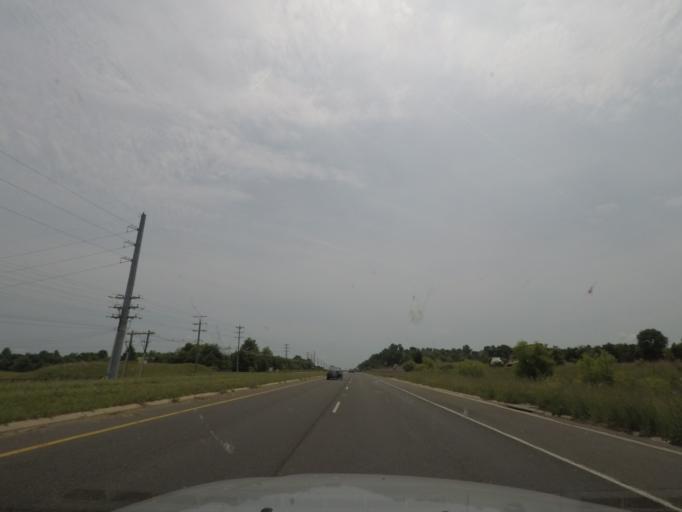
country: US
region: Virginia
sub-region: Prince William County
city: Bull Run Mountain Estates
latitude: 38.8674
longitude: -77.6362
